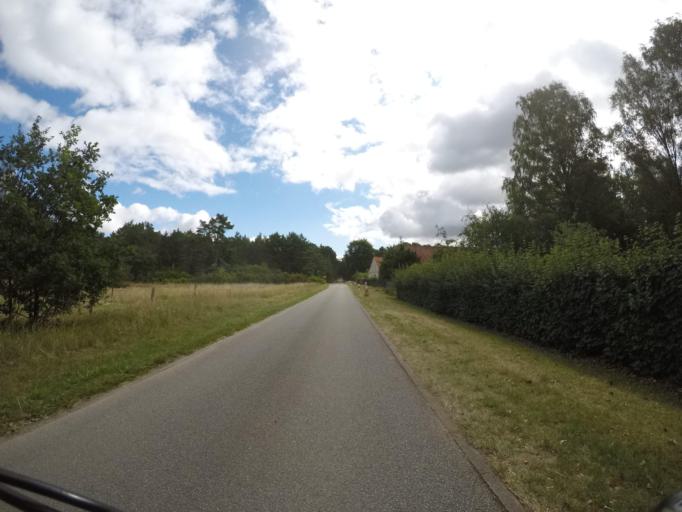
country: DE
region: Lower Saxony
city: Hitzacker
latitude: 53.2262
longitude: 10.9935
